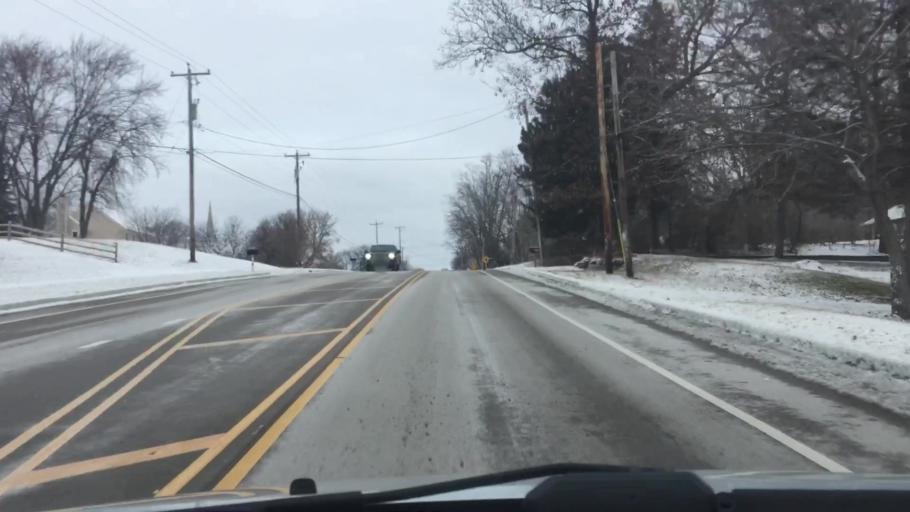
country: US
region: Wisconsin
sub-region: Waukesha County
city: Brookfield
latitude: 43.0761
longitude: -88.1059
